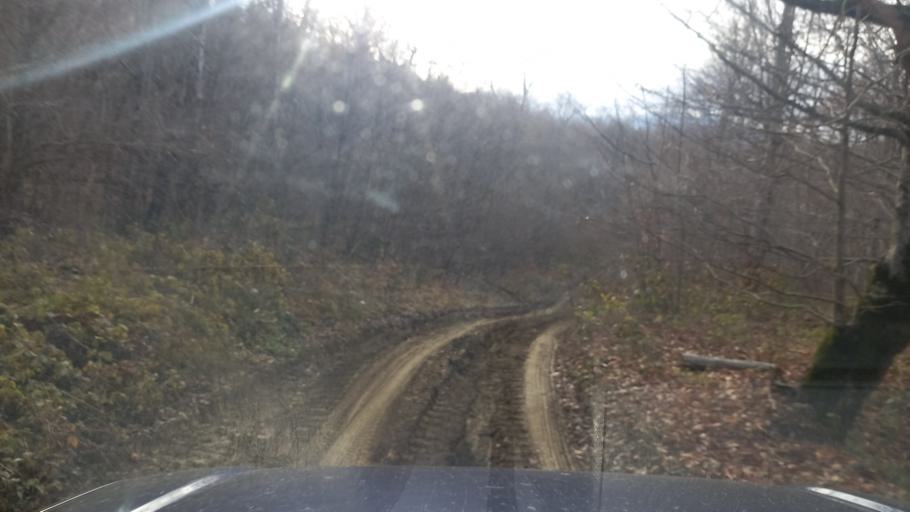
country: RU
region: Krasnodarskiy
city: Neftegorsk
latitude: 44.2021
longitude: 39.7035
